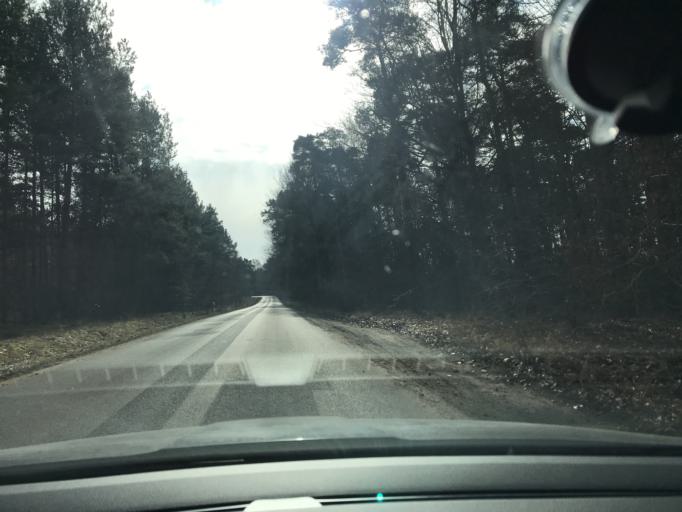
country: DE
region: Brandenburg
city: Erkner
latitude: 52.3952
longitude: 13.7646
